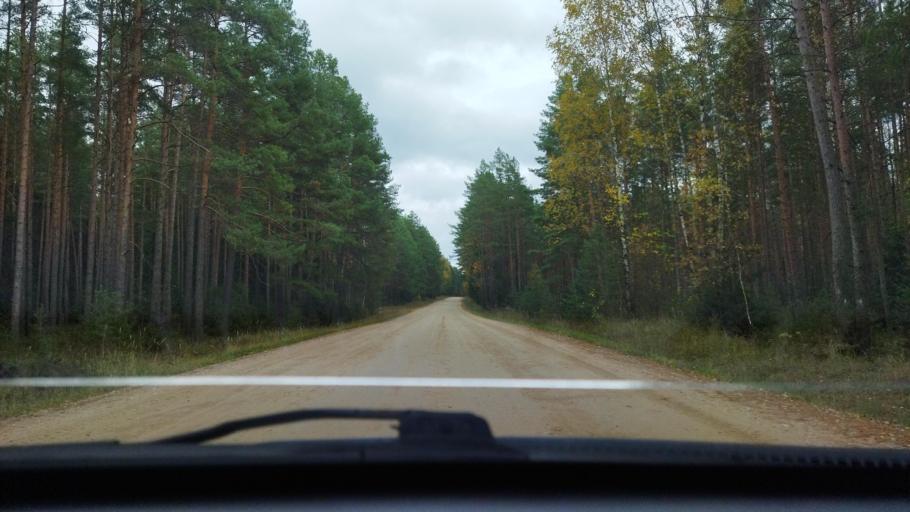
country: BY
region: Minsk
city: Svir
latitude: 54.8033
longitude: 26.2615
